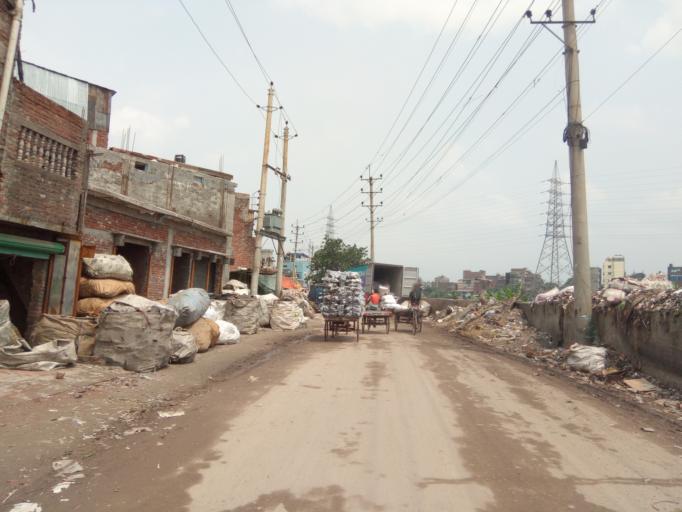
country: BD
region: Dhaka
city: Azimpur
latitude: 23.7129
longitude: 90.3865
